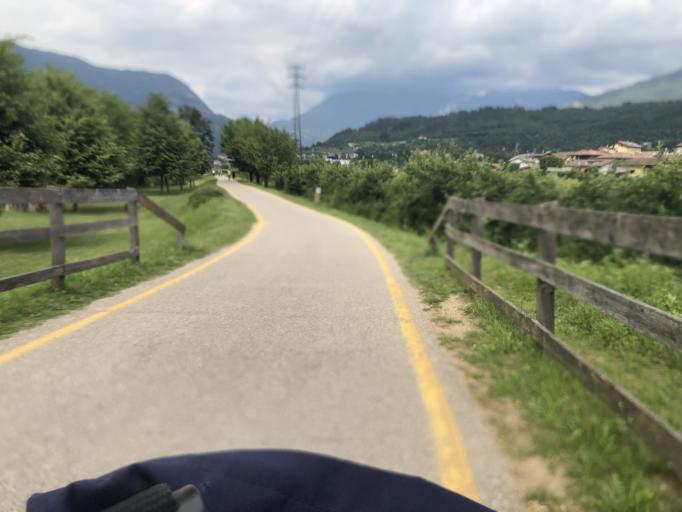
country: IT
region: Trentino-Alto Adige
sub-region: Provincia di Trento
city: Nogaredo
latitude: 45.8987
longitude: 11.0276
